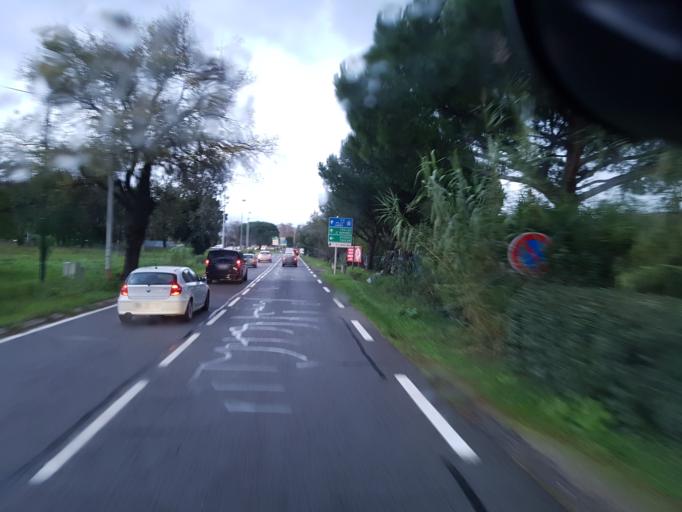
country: FR
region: Provence-Alpes-Cote d'Azur
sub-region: Departement du Var
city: Gassin
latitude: 43.2602
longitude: 6.5765
